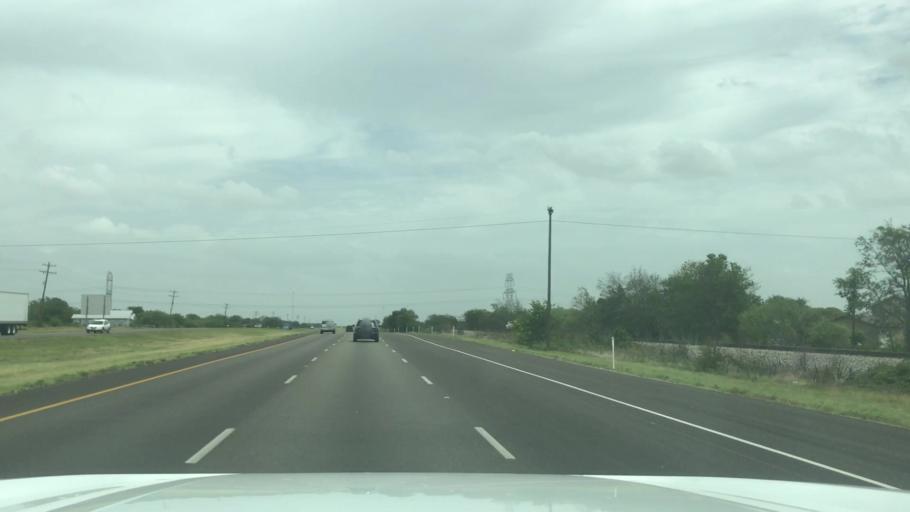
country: US
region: Texas
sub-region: McLennan County
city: Riesel
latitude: 31.5204
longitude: -96.9861
